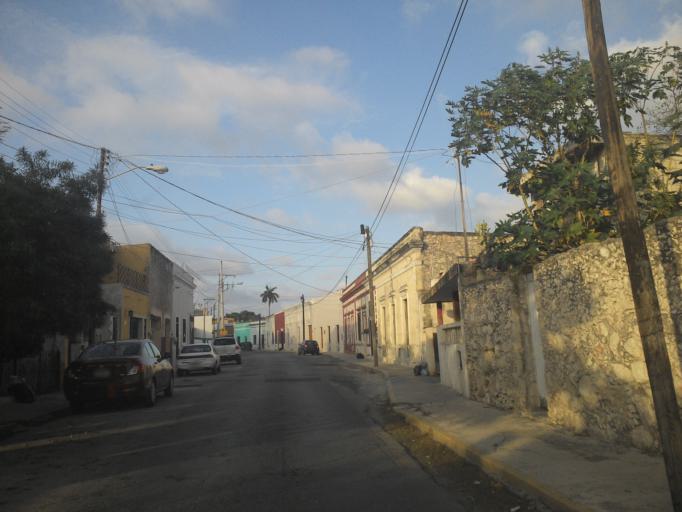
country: MX
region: Yucatan
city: Merida
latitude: 20.9651
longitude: -89.6323
